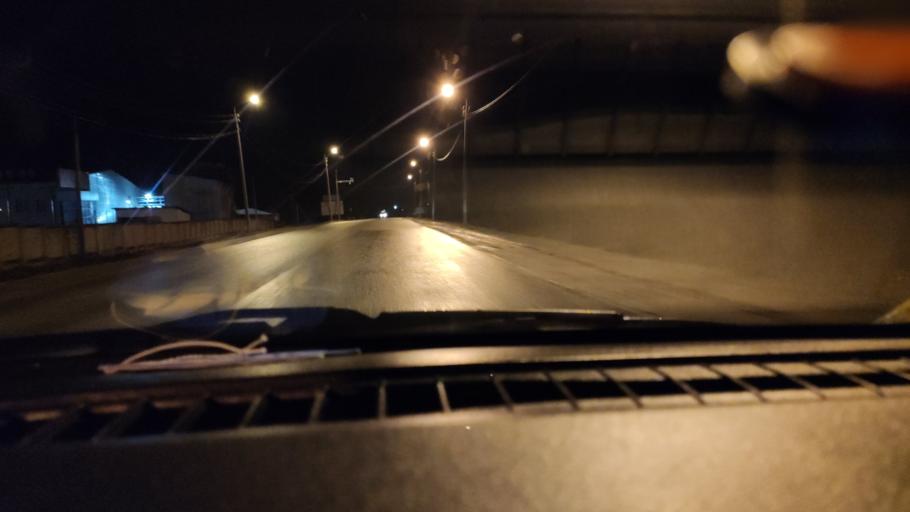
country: RU
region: Udmurtiya
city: Pirogovo
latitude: 56.7336
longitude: 53.2754
